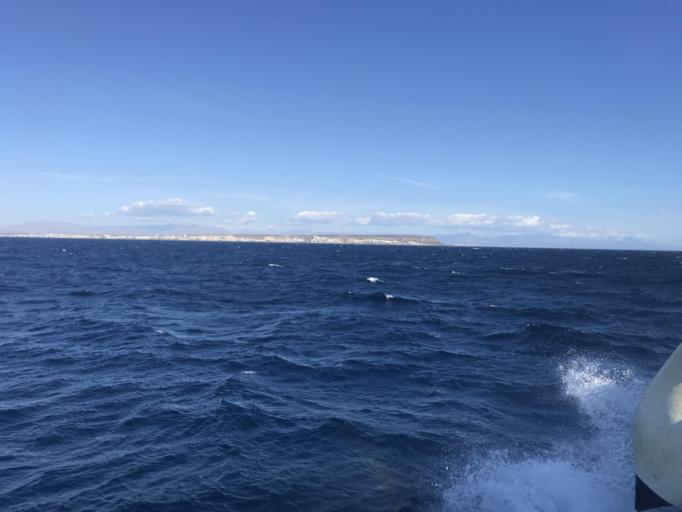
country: ES
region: Valencia
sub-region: Provincia de Alicante
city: Santa Pola
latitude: 38.1342
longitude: -0.5320
